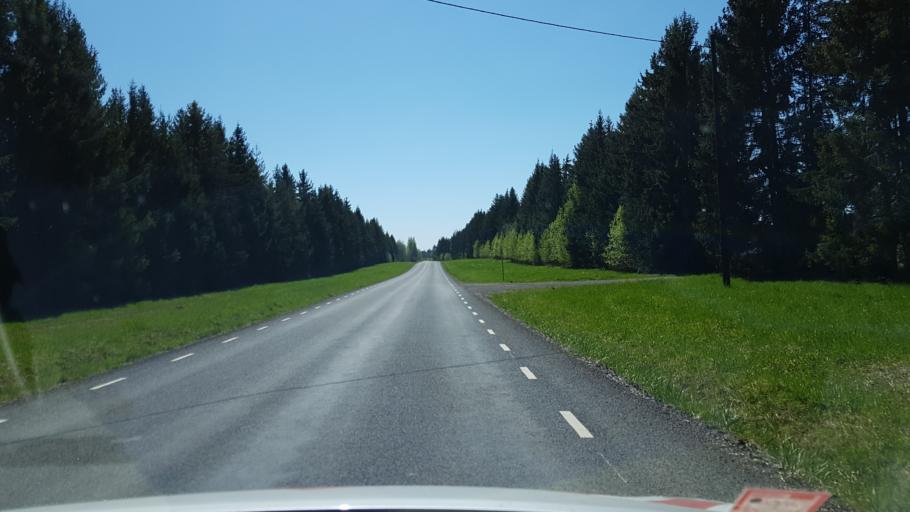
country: EE
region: Vorumaa
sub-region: Voru linn
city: Voru
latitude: 57.9485
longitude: 26.9554
